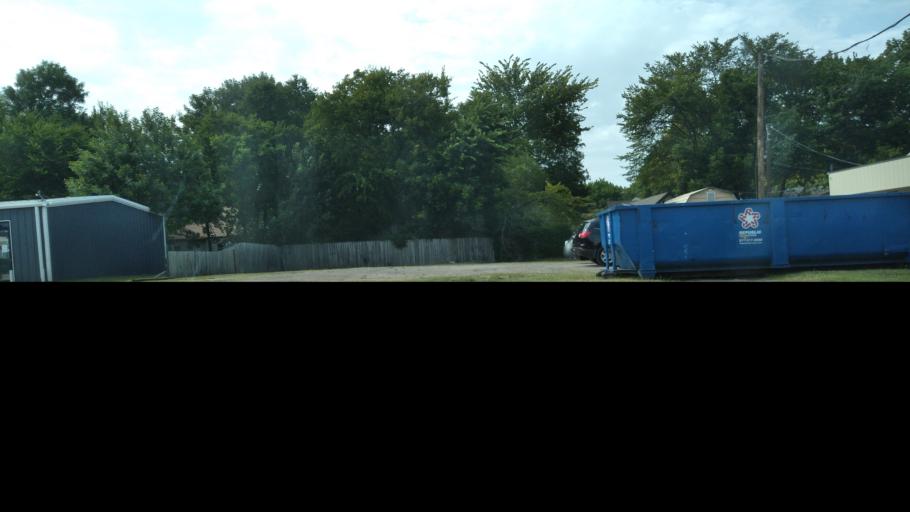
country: US
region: Texas
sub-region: Navarro County
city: Corsicana
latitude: 32.0853
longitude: -96.4763
